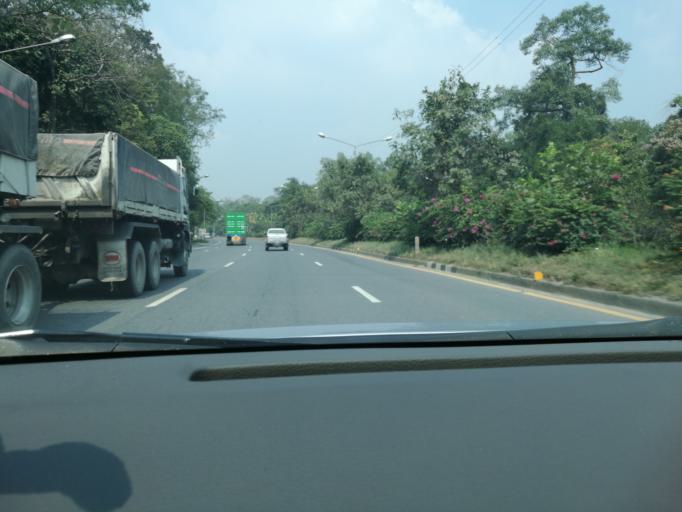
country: TH
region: Sara Buri
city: Chaloem Phra Kiat
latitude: 14.6679
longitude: 100.8875
